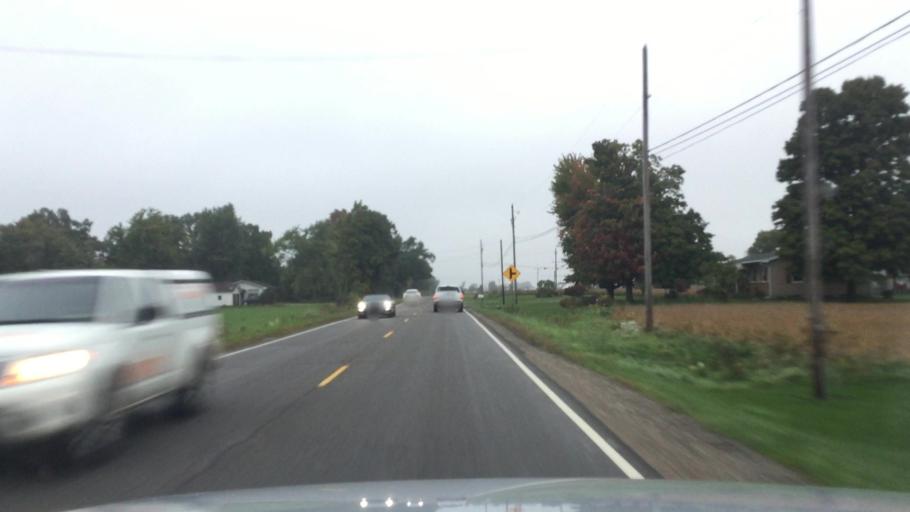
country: US
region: Michigan
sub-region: Shiawassee County
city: Corunna
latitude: 42.9070
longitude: -84.1237
